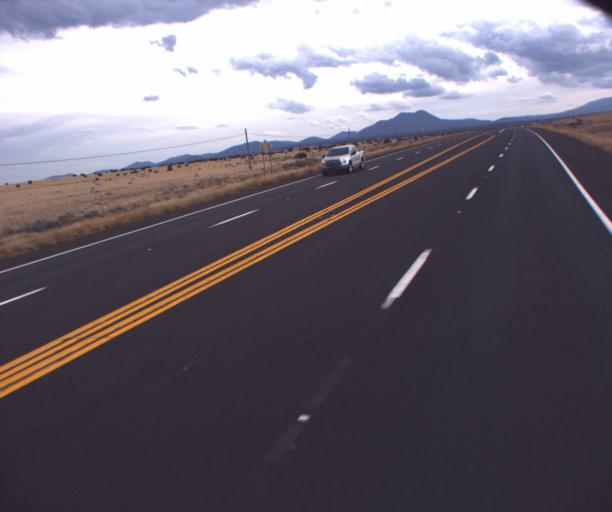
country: US
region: Arizona
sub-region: Coconino County
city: Flagstaff
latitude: 35.5779
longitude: -111.5303
